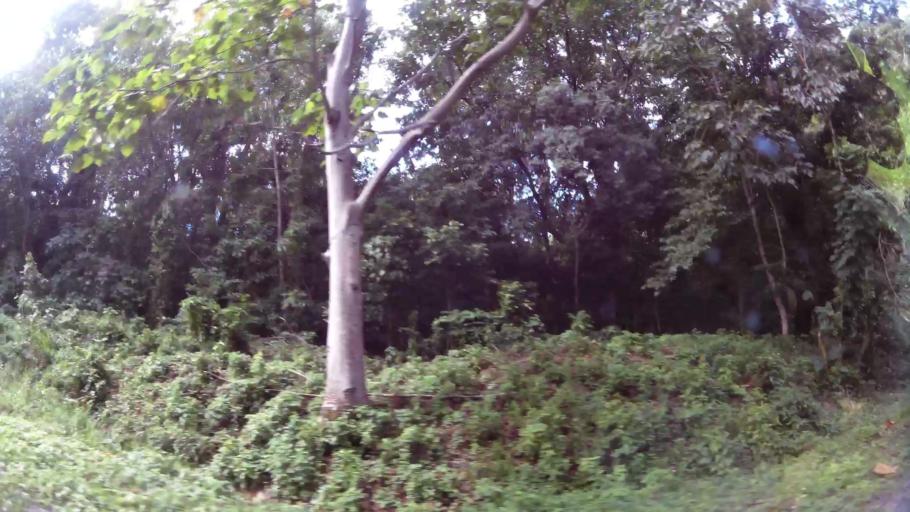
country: DM
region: Saint John
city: Portsmouth
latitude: 15.6206
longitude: -61.4622
